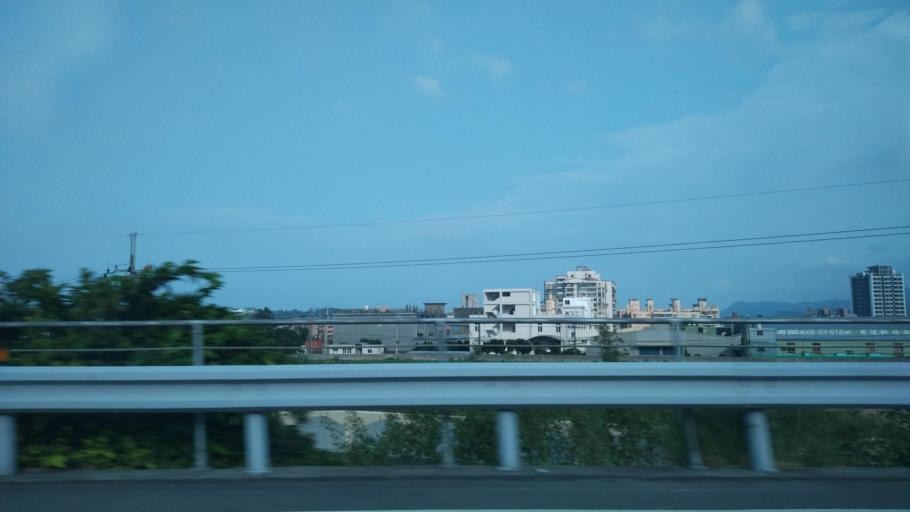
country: TW
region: Taiwan
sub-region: Keelung
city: Keelung
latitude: 25.2269
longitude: 121.6294
